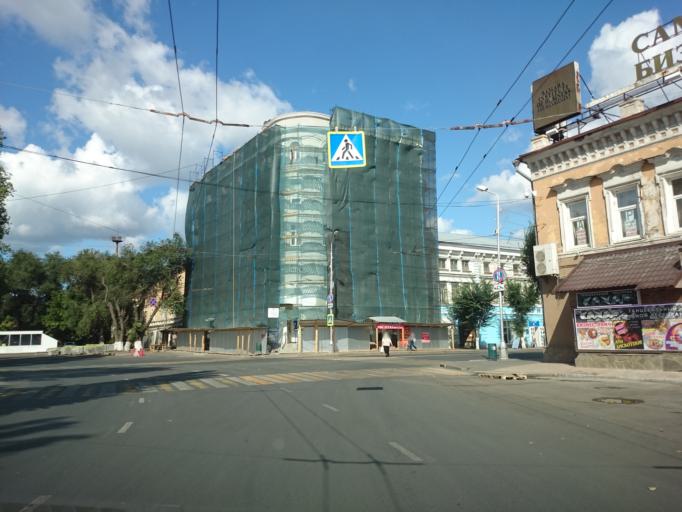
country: RU
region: Samara
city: Rozhdestveno
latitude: 53.1859
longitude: 50.0883
